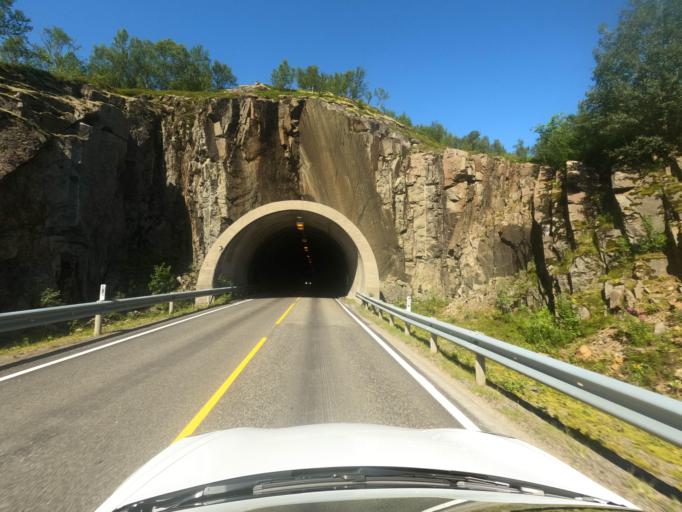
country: NO
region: Nordland
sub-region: Hadsel
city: Stokmarknes
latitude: 68.4391
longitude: 14.9830
